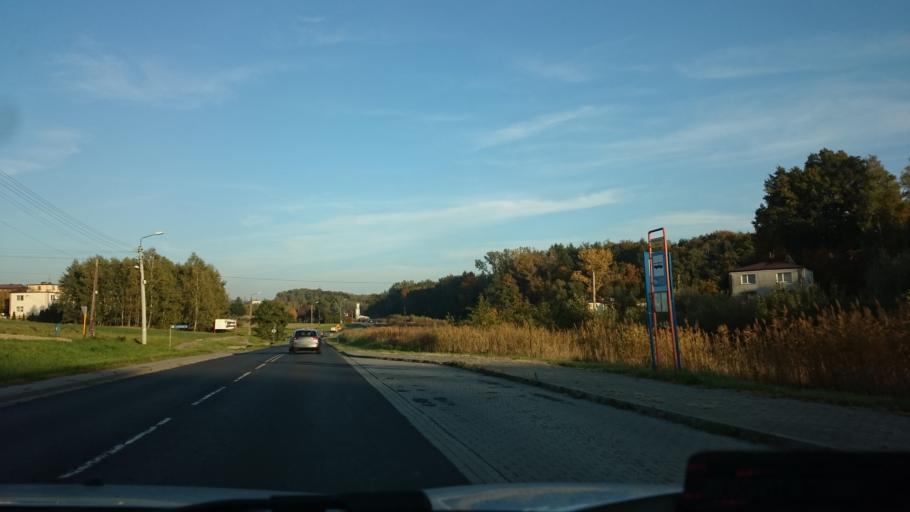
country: PL
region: Silesian Voivodeship
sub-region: Powiat wodzislawski
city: Marklowice
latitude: 50.0155
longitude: 18.5447
